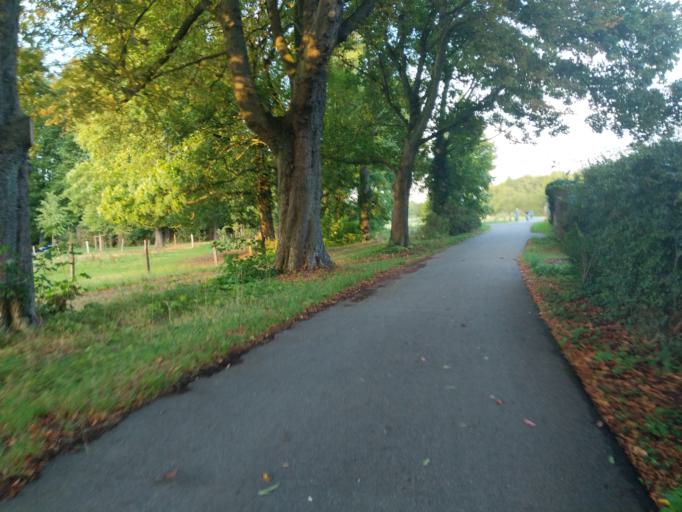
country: DE
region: North Rhine-Westphalia
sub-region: Regierungsbezirk Dusseldorf
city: Krefeld
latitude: 51.3346
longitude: 6.6508
